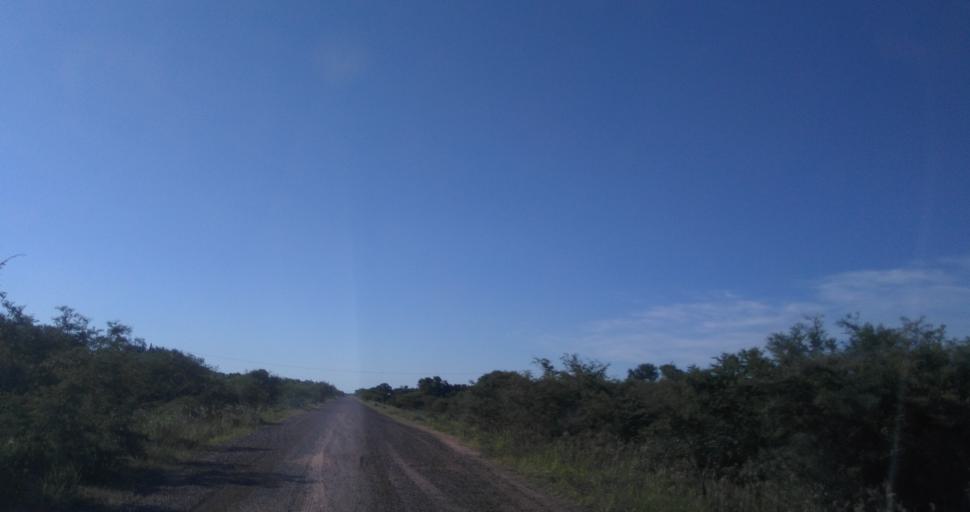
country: AR
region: Chaco
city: Barranqueras
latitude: -27.4207
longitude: -58.9345
